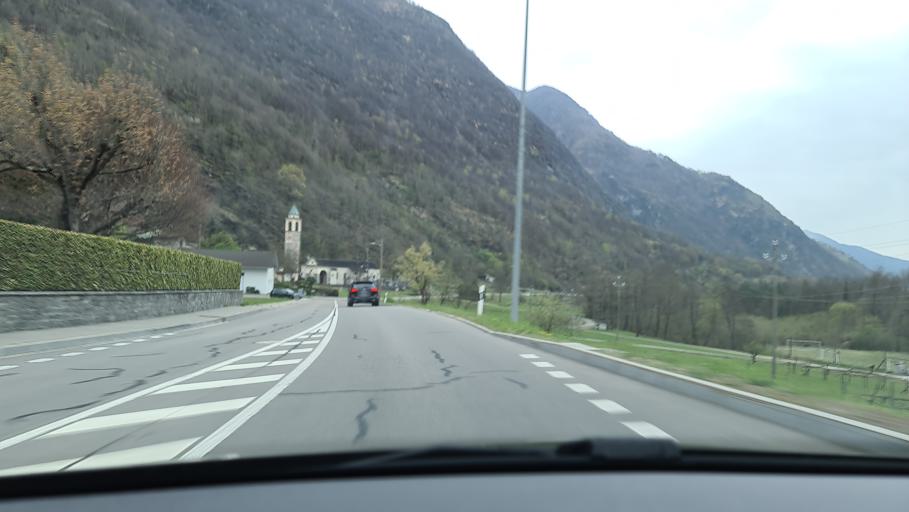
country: CH
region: Ticino
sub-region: Vallemaggia District
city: Cevio
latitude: 46.2866
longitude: 8.6619
